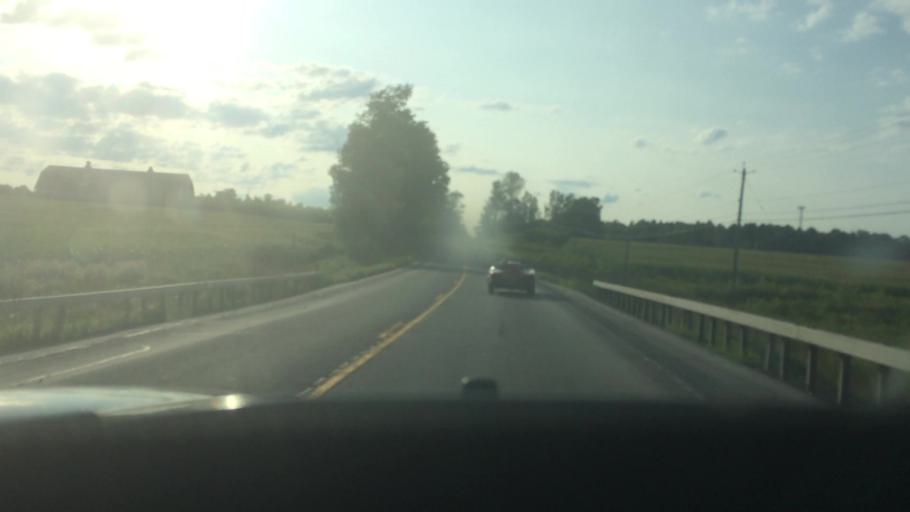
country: US
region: New York
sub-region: St. Lawrence County
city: Canton
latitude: 44.6477
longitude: -75.2870
